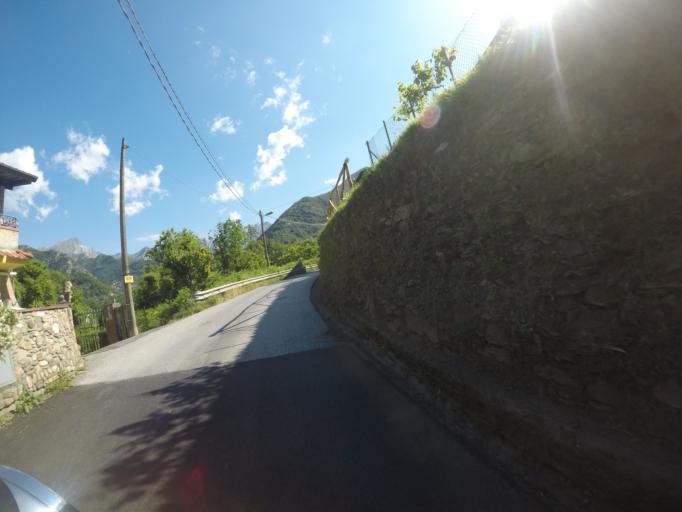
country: IT
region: Tuscany
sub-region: Provincia di Massa-Carrara
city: Montignoso
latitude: 44.0521
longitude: 10.1675
